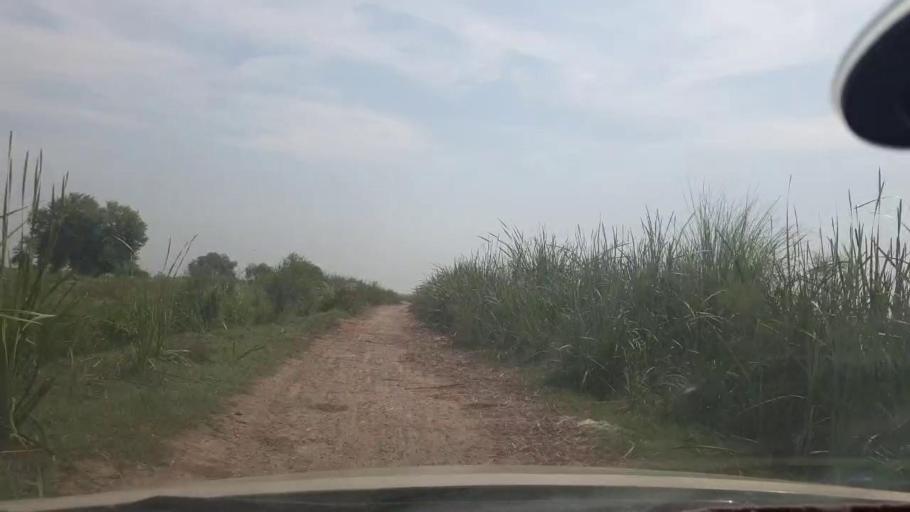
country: PK
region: Sindh
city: Jacobabad
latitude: 28.3180
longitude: 68.4901
